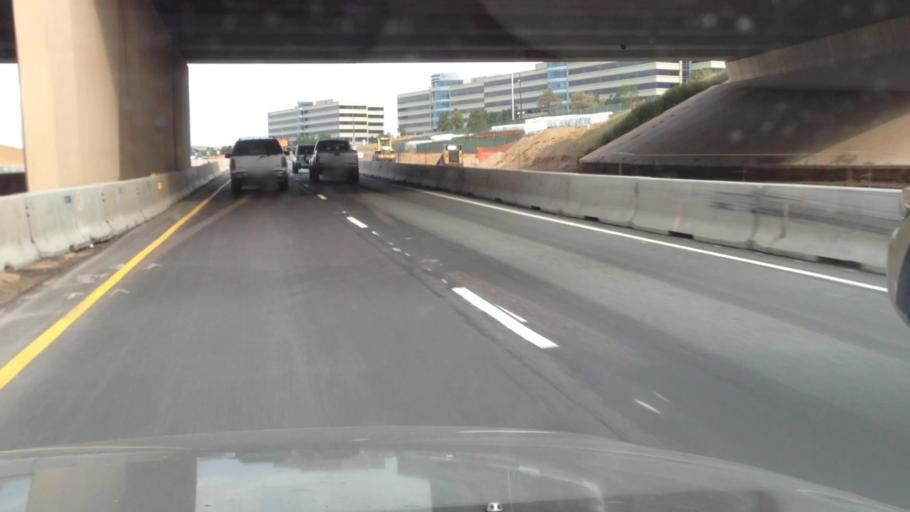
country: US
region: Colorado
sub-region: Douglas County
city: Highlands Ranch
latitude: 39.5600
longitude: -105.0084
